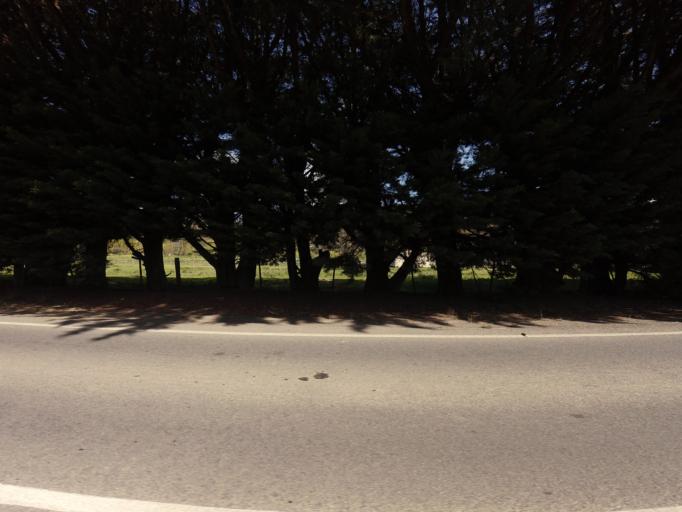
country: AU
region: Tasmania
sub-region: Derwent Valley
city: New Norfolk
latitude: -42.7780
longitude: 147.0412
